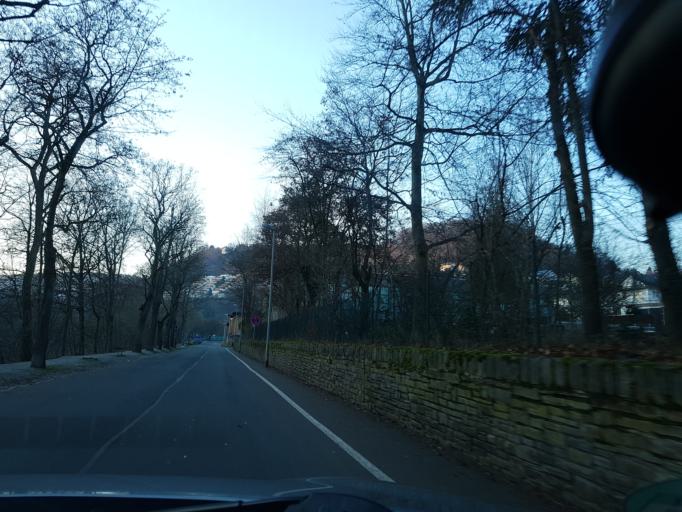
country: DE
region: Rheinland-Pfalz
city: Bad Ems
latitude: 50.3341
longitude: 7.7077
